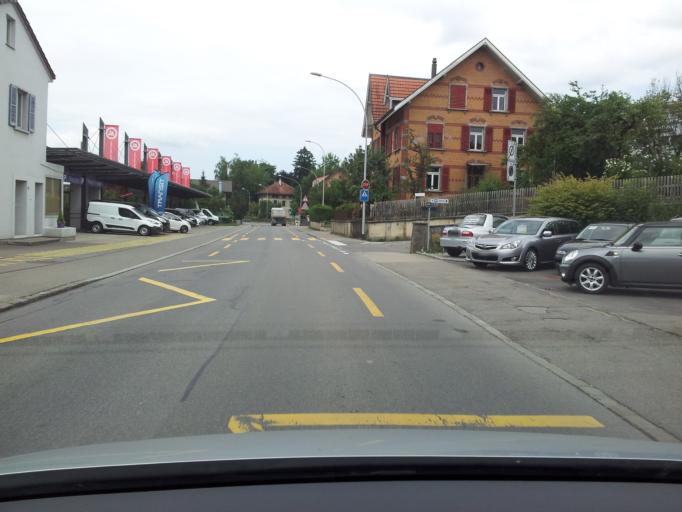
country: CH
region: Lucerne
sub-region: Sursee District
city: Sursee
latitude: 47.1686
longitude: 8.1139
